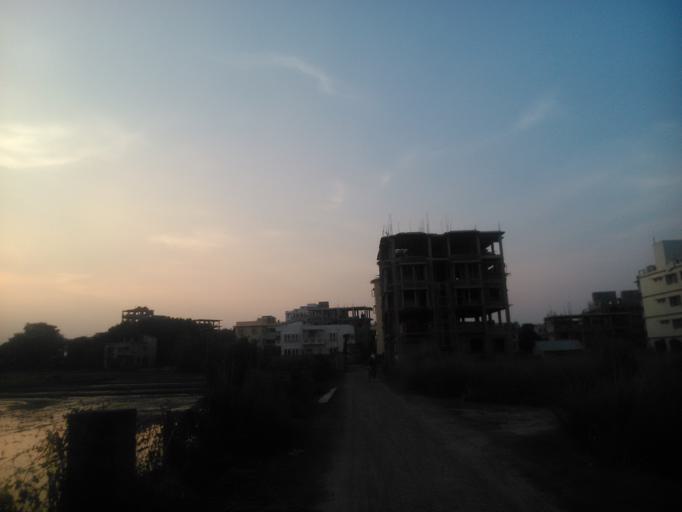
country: IN
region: West Bengal
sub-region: Nadia
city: Navadwip
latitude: 23.4305
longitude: 88.3904
